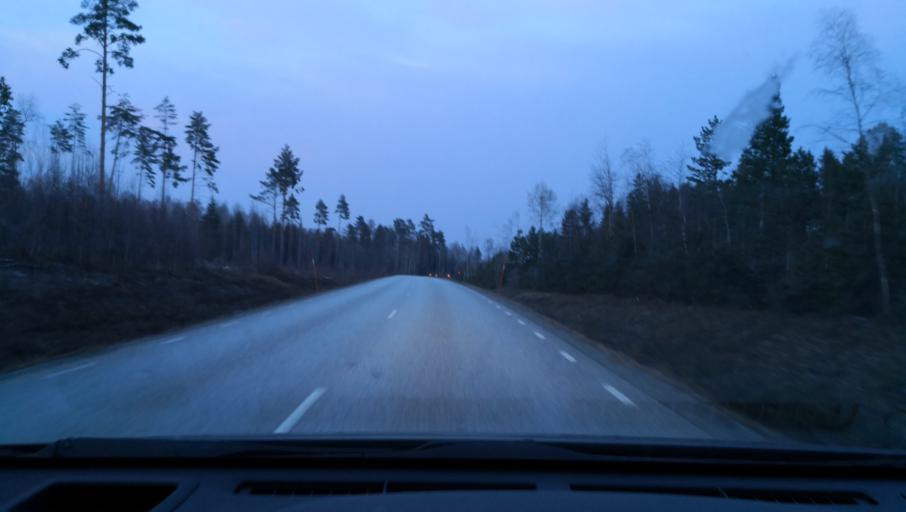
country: SE
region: OErebro
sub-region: Lindesbergs Kommun
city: Lindesberg
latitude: 59.5920
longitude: 15.2762
